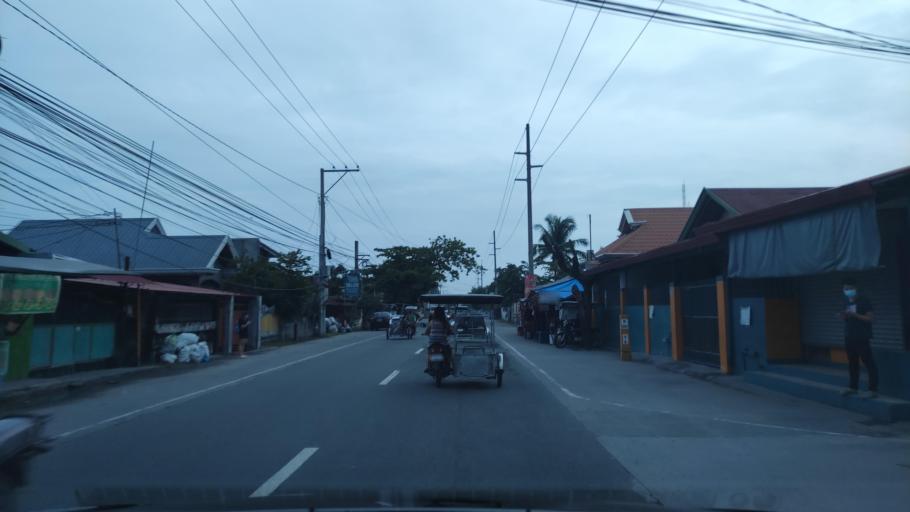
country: PH
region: Central Luzon
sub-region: Province of Pampanga
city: Santa Ana
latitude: 15.1048
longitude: 120.7710
